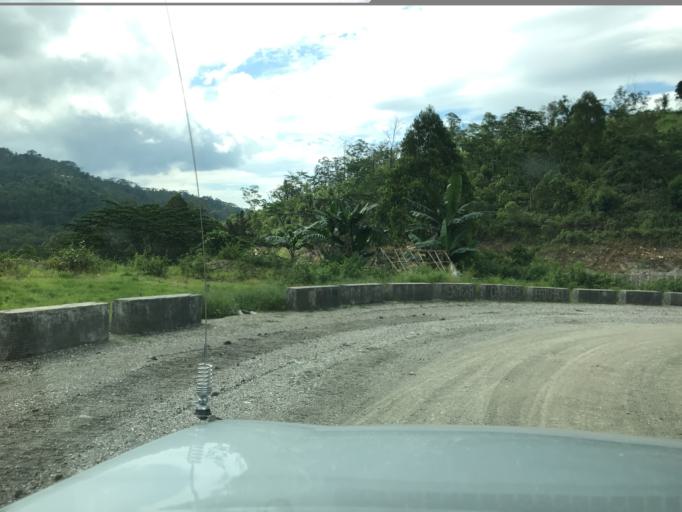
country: TL
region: Aileu
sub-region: Aileu Villa
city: Aileu
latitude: -8.6595
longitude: 125.5318
